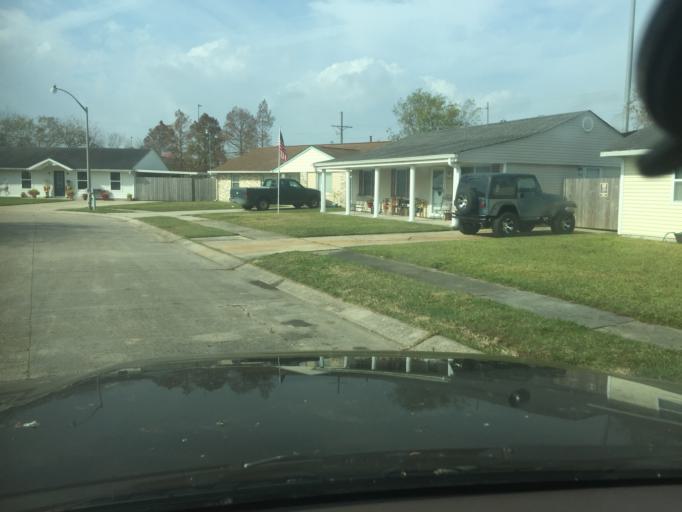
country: US
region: Louisiana
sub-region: Jefferson Parish
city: Avondale
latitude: 29.9156
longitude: -90.1992
